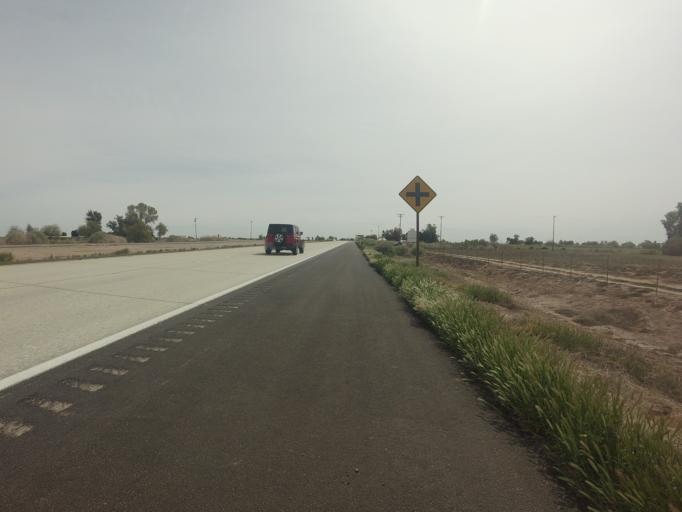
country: US
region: California
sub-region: Imperial County
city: Brawley
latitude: 32.9877
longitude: -115.5804
